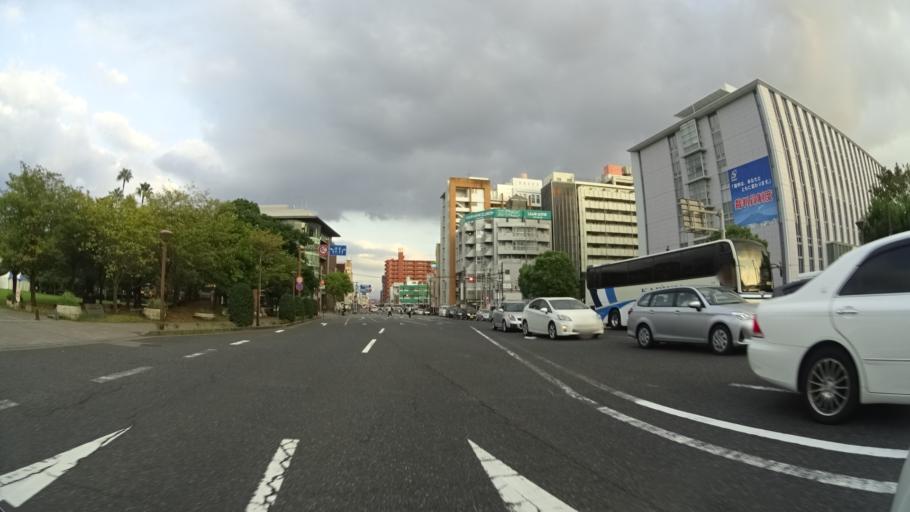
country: JP
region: Kagoshima
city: Kagoshima-shi
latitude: 31.5986
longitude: 130.5571
